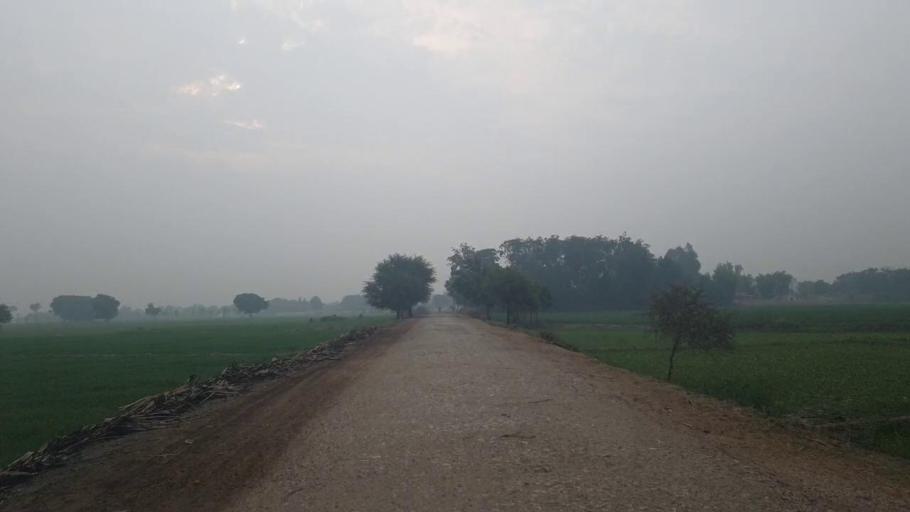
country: PK
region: Sindh
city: Tando Adam
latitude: 25.7340
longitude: 68.6710
